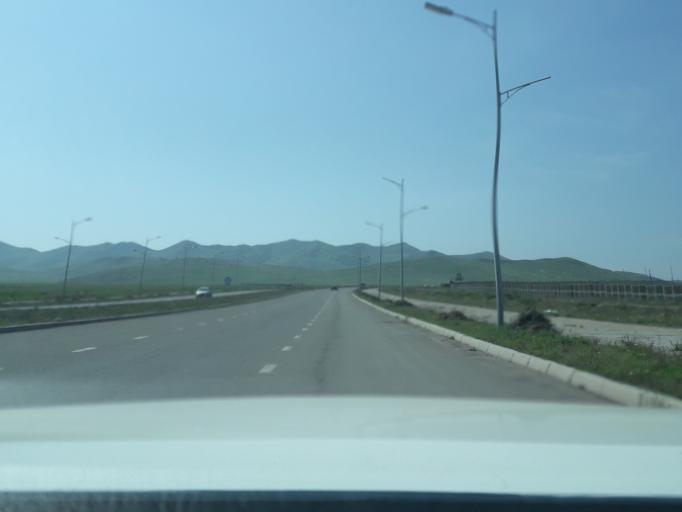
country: MN
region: Ulaanbaatar
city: Ulaanbaatar
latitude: 47.8330
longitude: 106.7870
